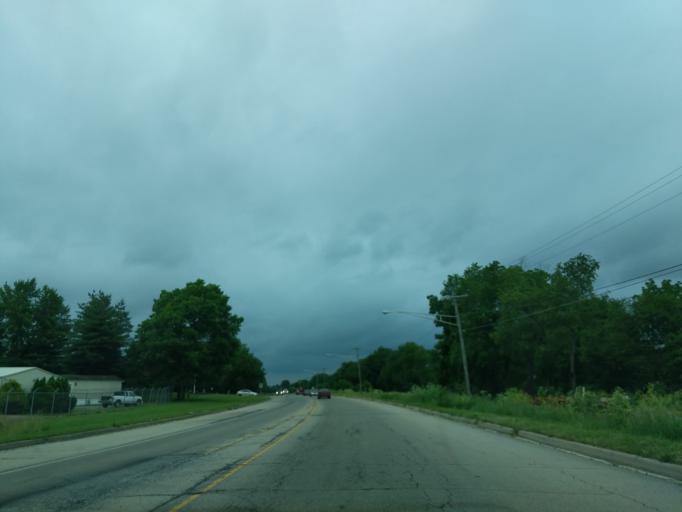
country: US
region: Indiana
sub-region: Madison County
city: Chesterfield
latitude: 40.1138
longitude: -85.5790
